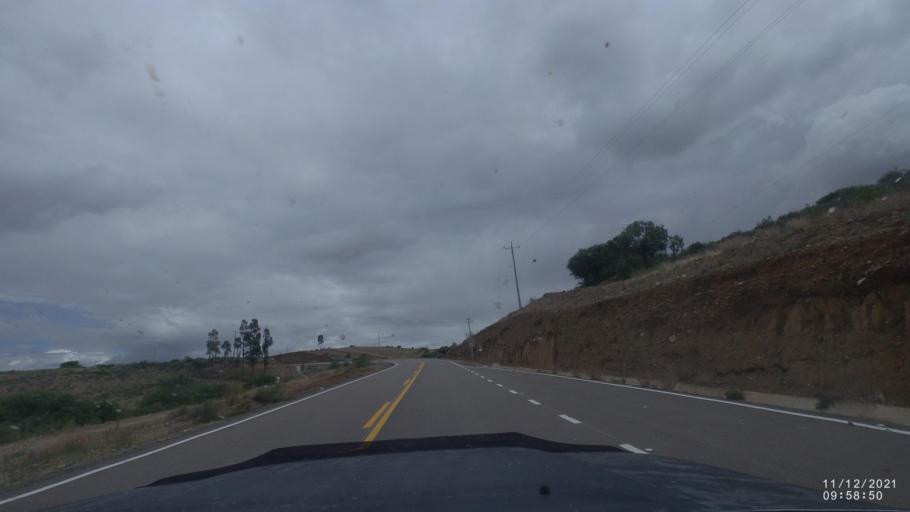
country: BO
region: Cochabamba
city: Cliza
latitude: -17.7508
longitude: -65.9159
